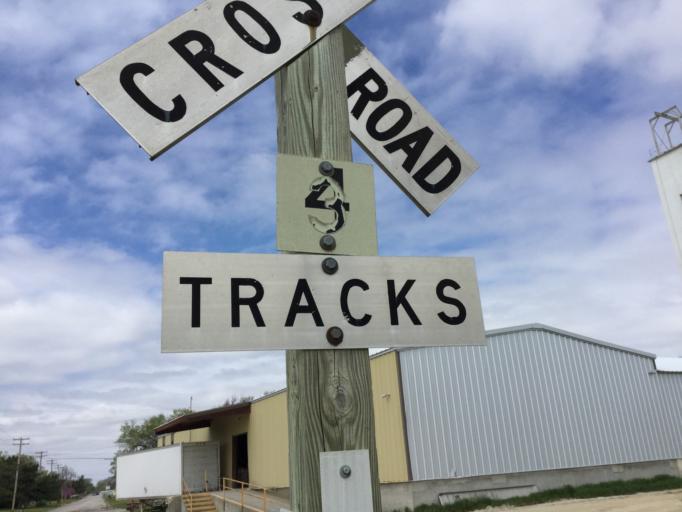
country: US
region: Kansas
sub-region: Osborne County
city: Osborne
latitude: 39.4367
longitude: -98.6892
